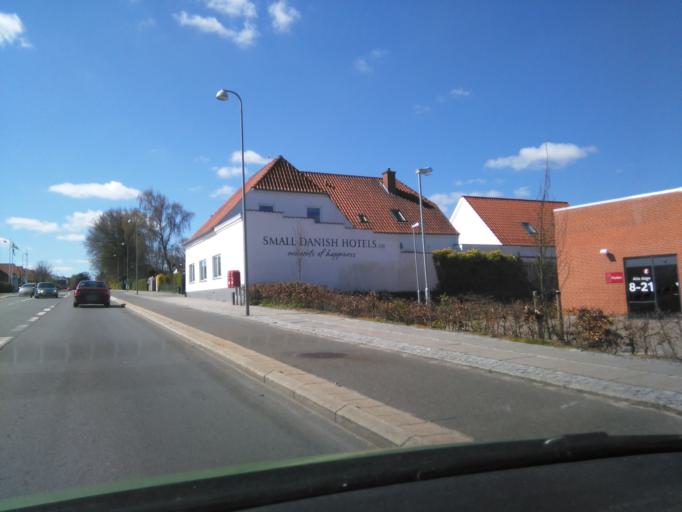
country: DK
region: Central Jutland
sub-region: Horsens Kommune
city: Horsens
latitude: 55.8509
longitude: 9.8292
